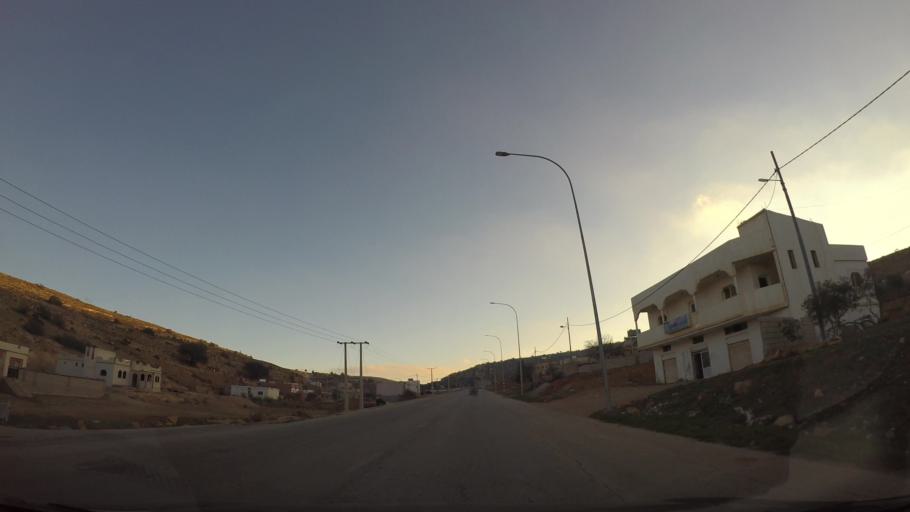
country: JO
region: Ma'an
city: Petra
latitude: 30.4194
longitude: 35.5106
